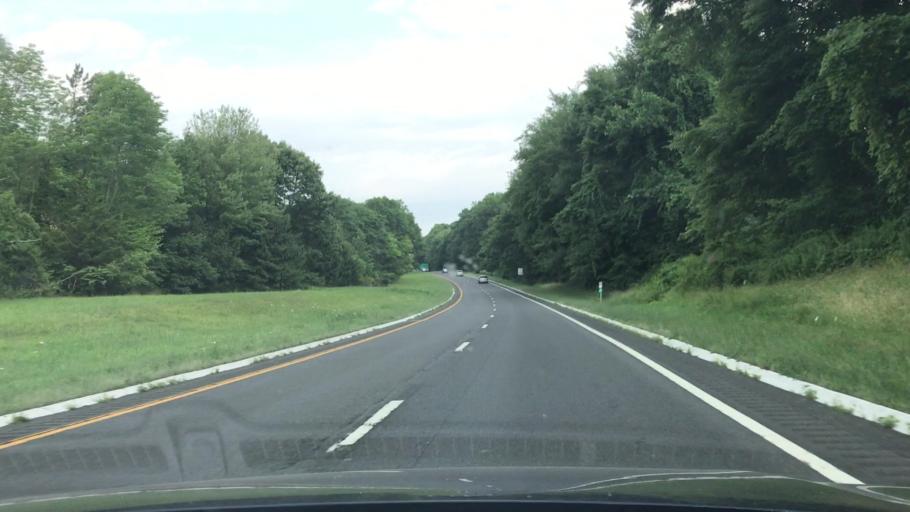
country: US
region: New York
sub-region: Rockland County
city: Blauvelt
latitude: 41.0625
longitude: -73.9762
